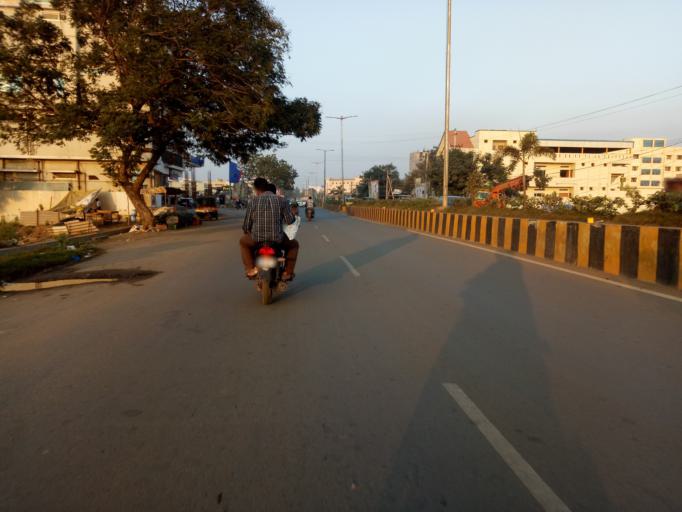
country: IN
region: Andhra Pradesh
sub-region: Nellore
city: Nellore
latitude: 14.4372
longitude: 79.9831
